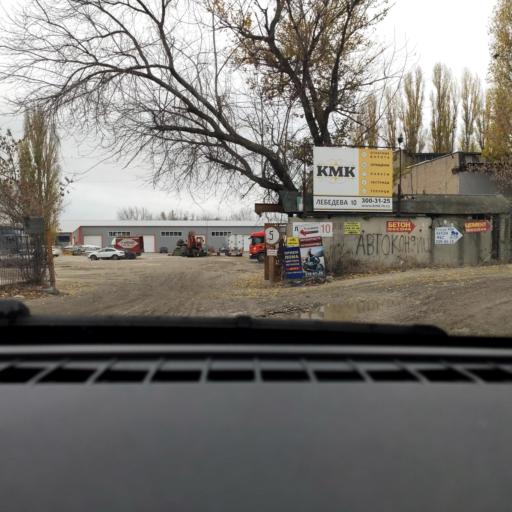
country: RU
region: Voronezj
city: Voronezh
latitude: 51.6231
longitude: 39.2286
